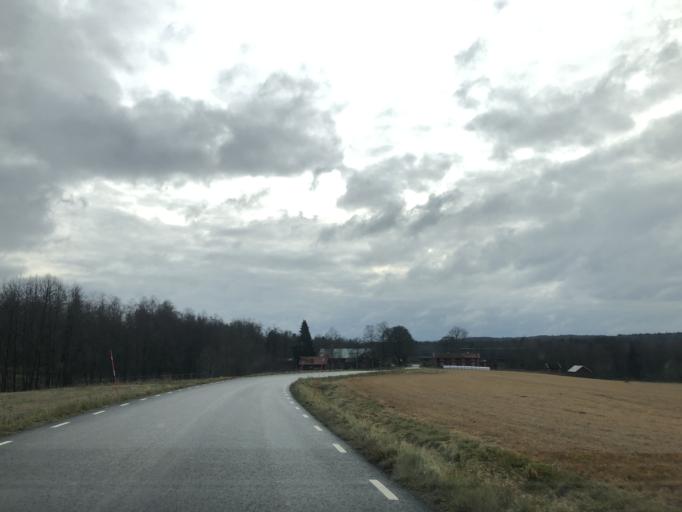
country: SE
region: Vaestra Goetaland
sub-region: Ulricehamns Kommun
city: Ulricehamn
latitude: 57.8145
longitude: 13.2438
